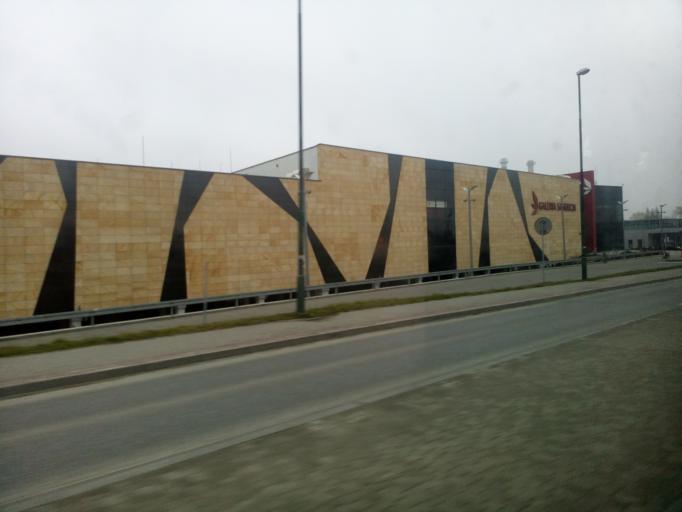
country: PL
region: Lesser Poland Voivodeship
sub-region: Powiat nowosadecki
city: Nowy Sacz
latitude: 49.5855
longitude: 20.6734
